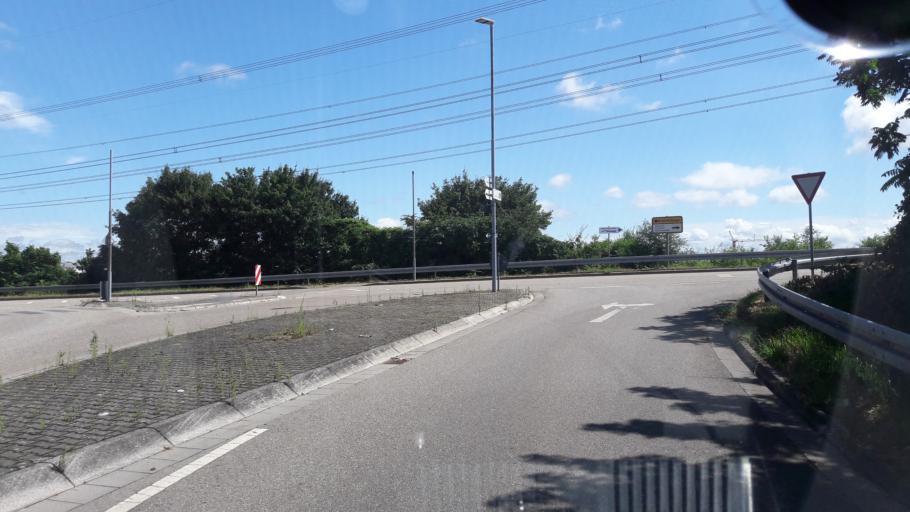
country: DE
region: Baden-Wuerttemberg
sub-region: Karlsruhe Region
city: Philippsburg
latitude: 49.2270
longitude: 8.4619
